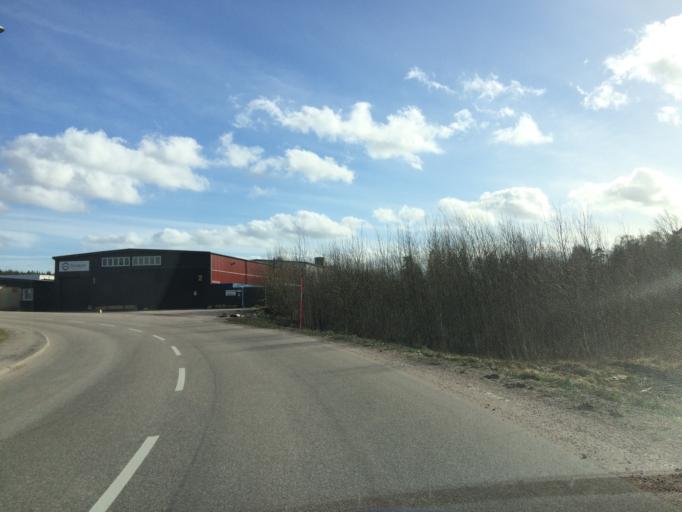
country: SE
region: Kronoberg
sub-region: Ljungby Kommun
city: Ljungby
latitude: 56.6919
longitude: 13.8685
